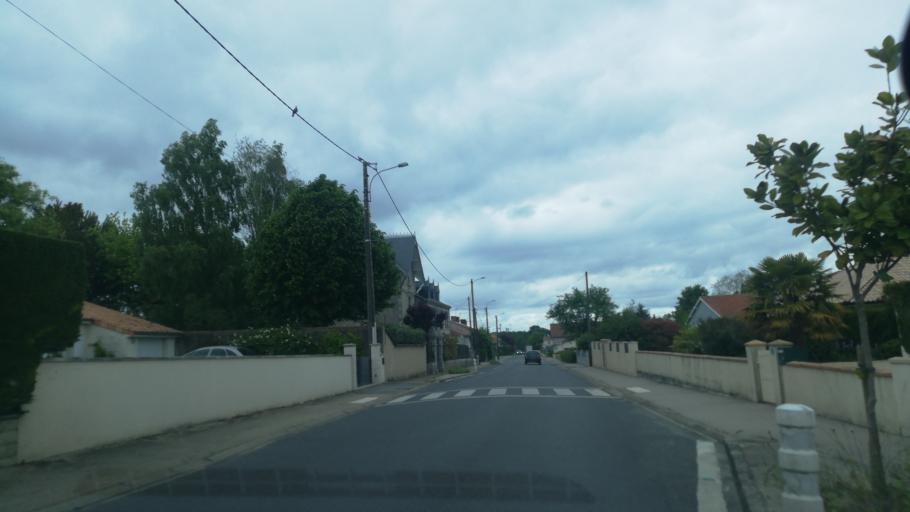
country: FR
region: Poitou-Charentes
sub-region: Departement des Deux-Sevres
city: La Chapelle-Saint-Laurent
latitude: 46.7513
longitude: -0.4749
